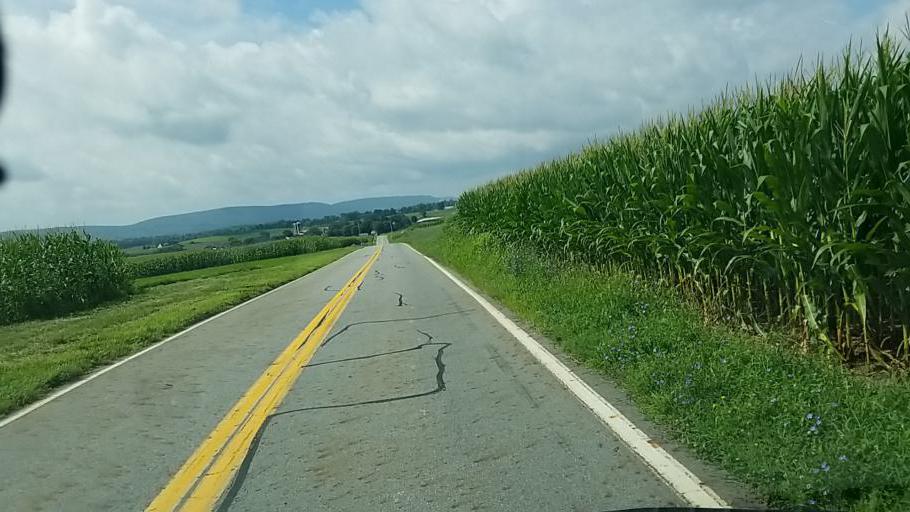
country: US
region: Pennsylvania
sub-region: Dauphin County
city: Millersburg
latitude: 40.5872
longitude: -76.8905
